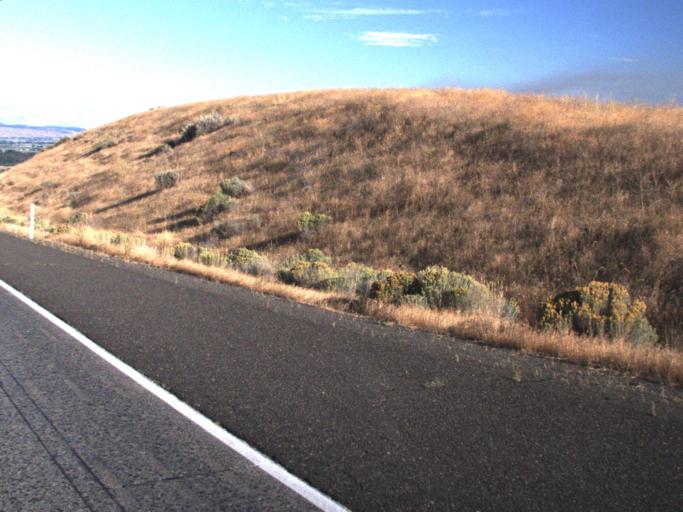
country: US
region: Washington
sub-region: Kittitas County
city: Kittitas
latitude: 46.9143
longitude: -120.4778
